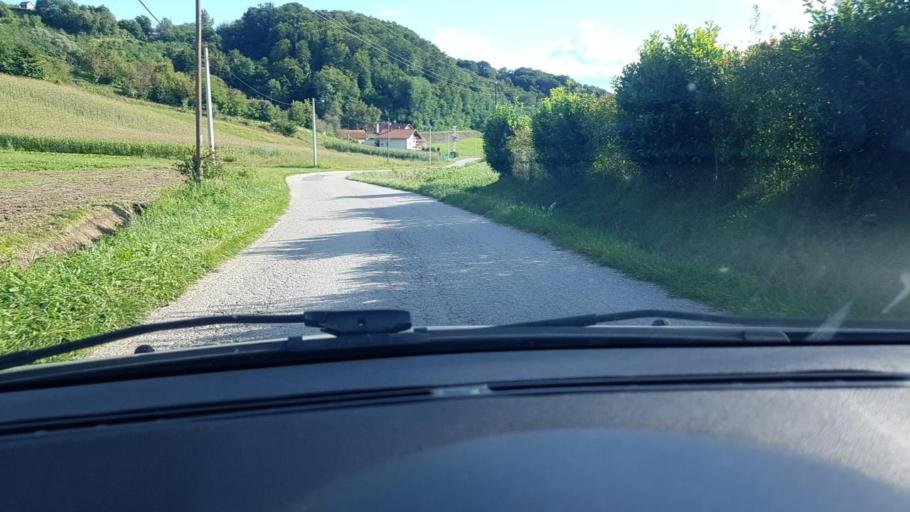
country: HR
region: Krapinsko-Zagorska
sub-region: Grad Krapina
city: Krapina
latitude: 46.1456
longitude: 15.8393
